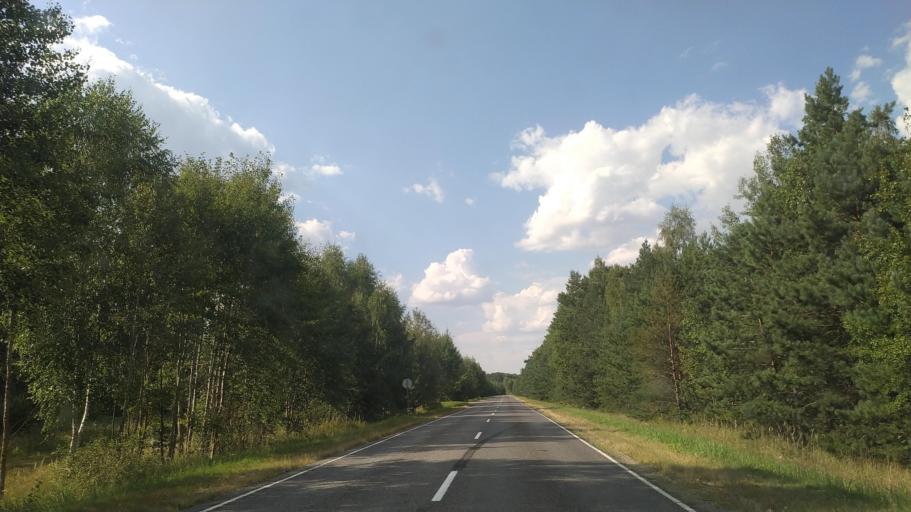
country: BY
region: Brest
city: Drahichyn
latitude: 52.2244
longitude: 25.1208
